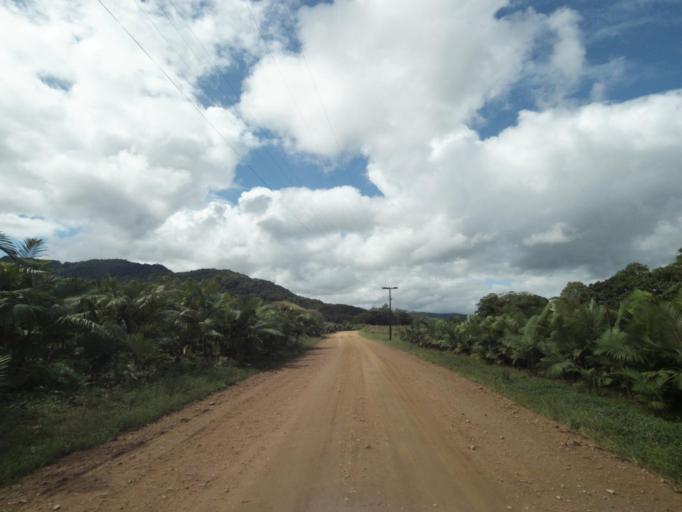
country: BR
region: Santa Catarina
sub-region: Pomerode
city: Pomerode
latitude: -26.6809
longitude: -49.1832
